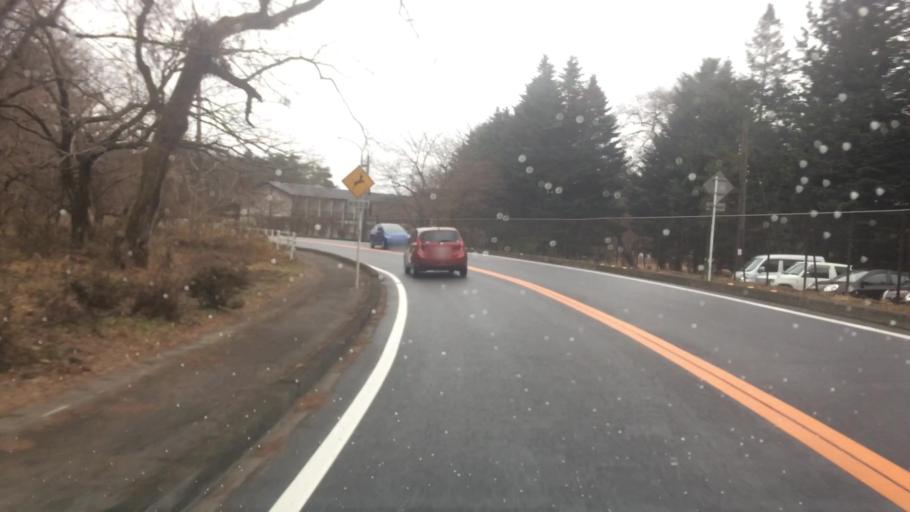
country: JP
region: Tochigi
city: Nikko
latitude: 36.7456
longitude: 139.6493
